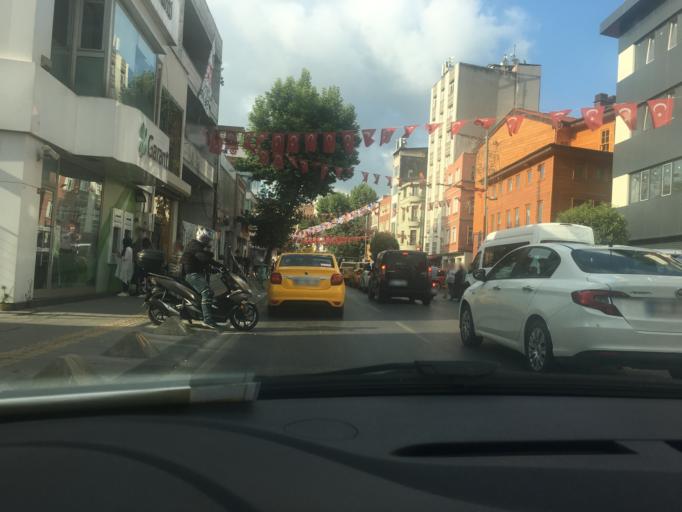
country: TR
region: Istanbul
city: Eminoenue
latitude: 41.0333
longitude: 28.9691
